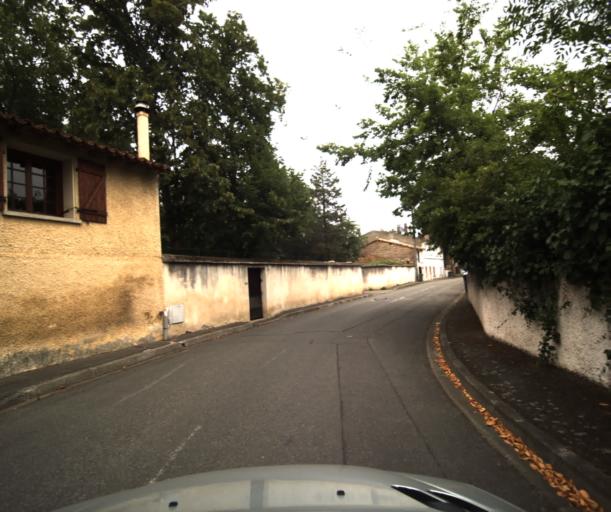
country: FR
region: Midi-Pyrenees
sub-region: Departement de la Haute-Garonne
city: Portet-sur-Garonne
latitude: 43.5233
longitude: 1.4091
